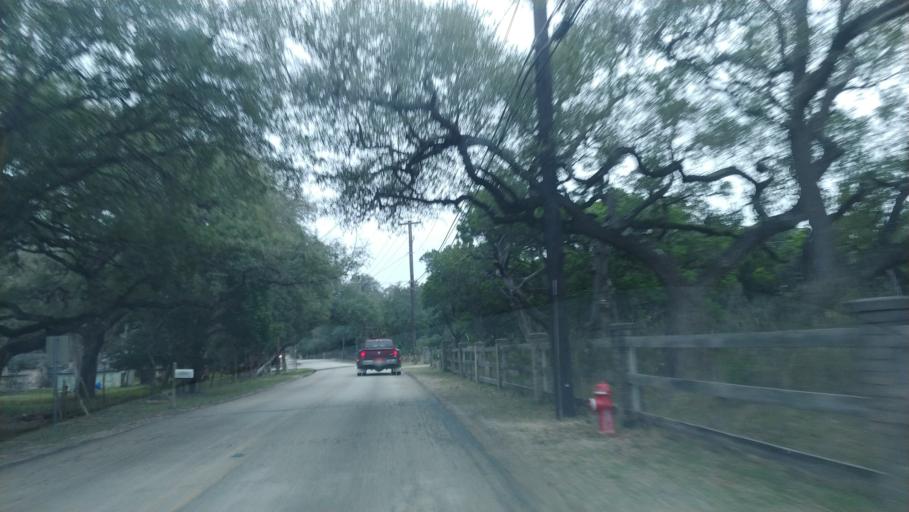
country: US
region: Texas
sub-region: Bexar County
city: Cross Mountain
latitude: 29.6205
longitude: -98.6851
